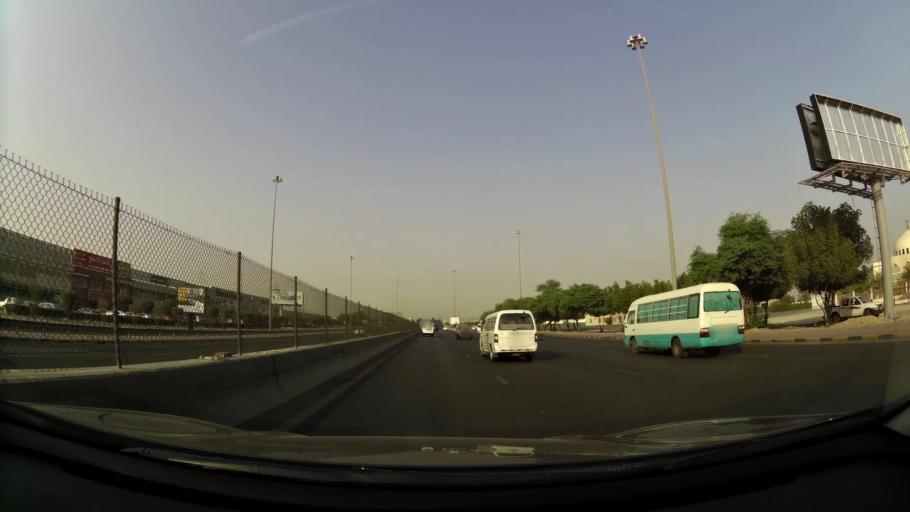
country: KW
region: Al Asimah
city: Ar Rabiyah
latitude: 29.3153
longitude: 47.9459
